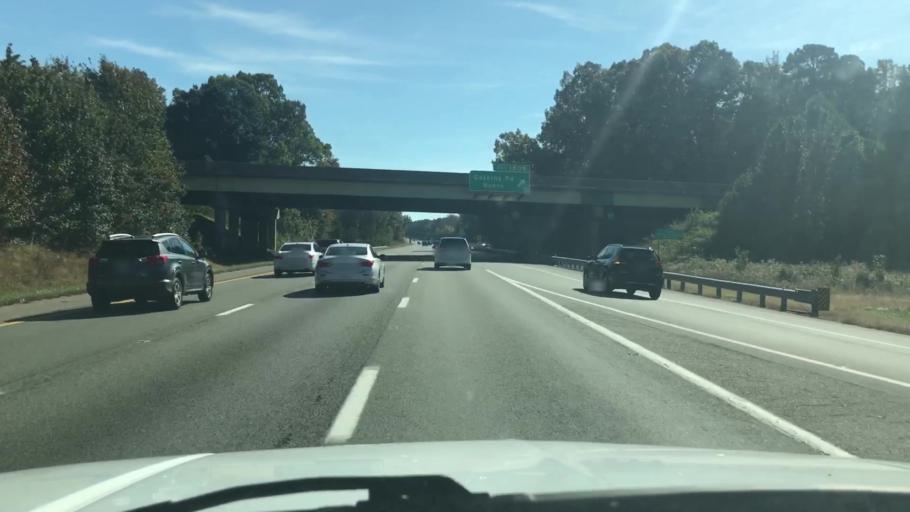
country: US
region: Virginia
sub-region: Henrico County
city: Short Pump
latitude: 37.6351
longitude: -77.5754
